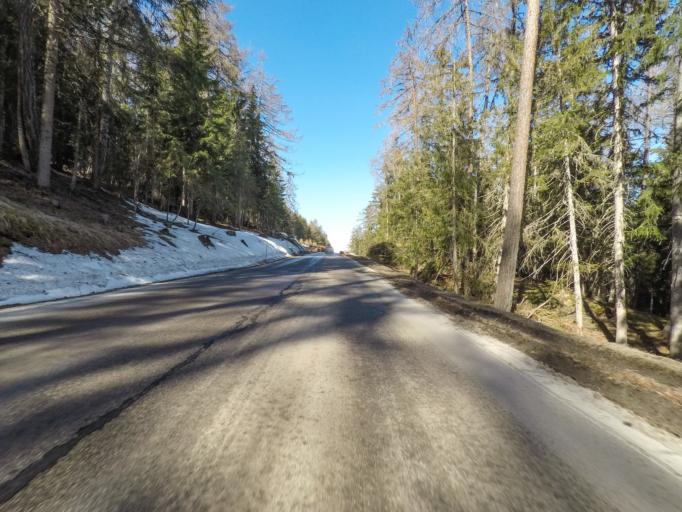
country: CH
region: Valais
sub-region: Herens District
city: Vex
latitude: 46.1989
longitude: 7.3802
